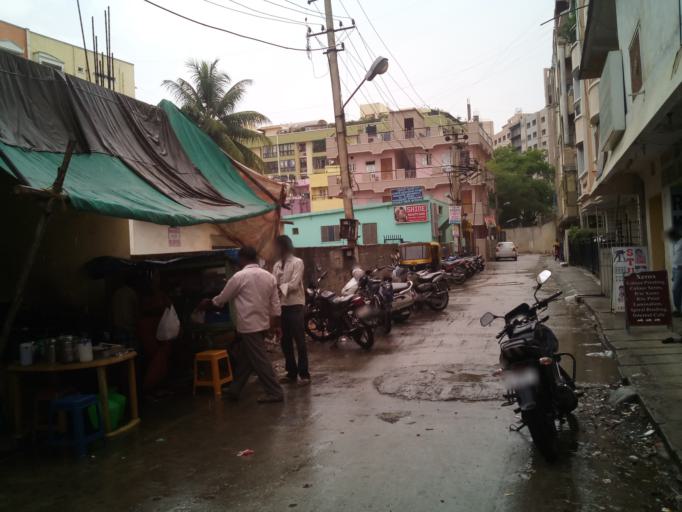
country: IN
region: Karnataka
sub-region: Bangalore Urban
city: Bangalore
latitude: 12.9943
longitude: 77.6636
